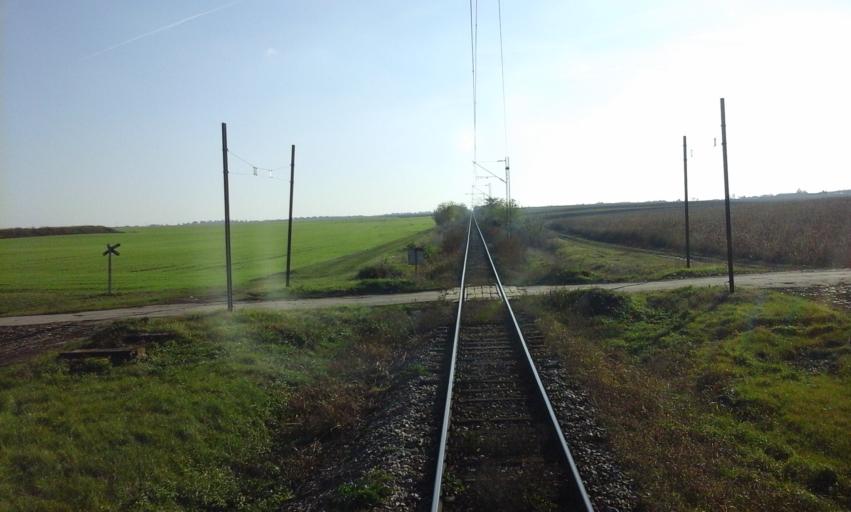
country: RS
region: Autonomna Pokrajina Vojvodina
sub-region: Severnobacki Okrug
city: Backa Topola
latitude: 45.7762
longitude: 19.6479
